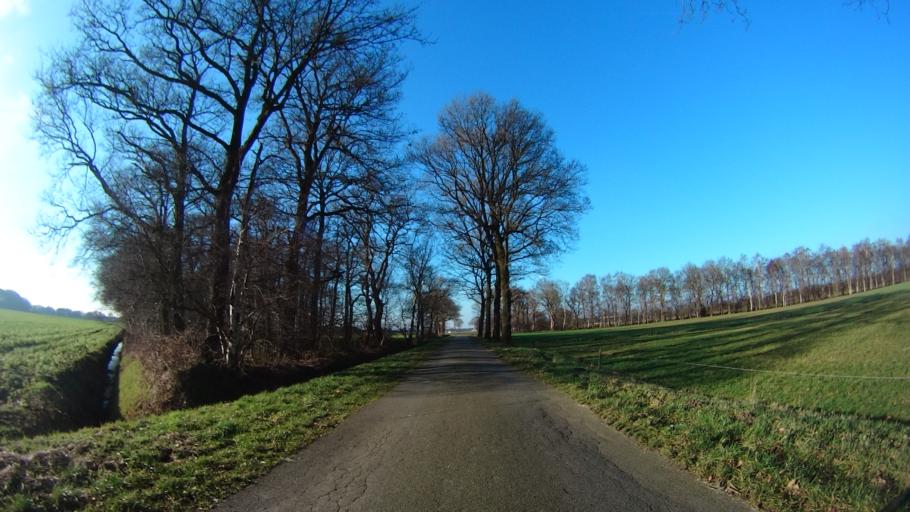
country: NL
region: Drenthe
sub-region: Gemeente Coevorden
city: Sleen
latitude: 52.7797
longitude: 6.8144
